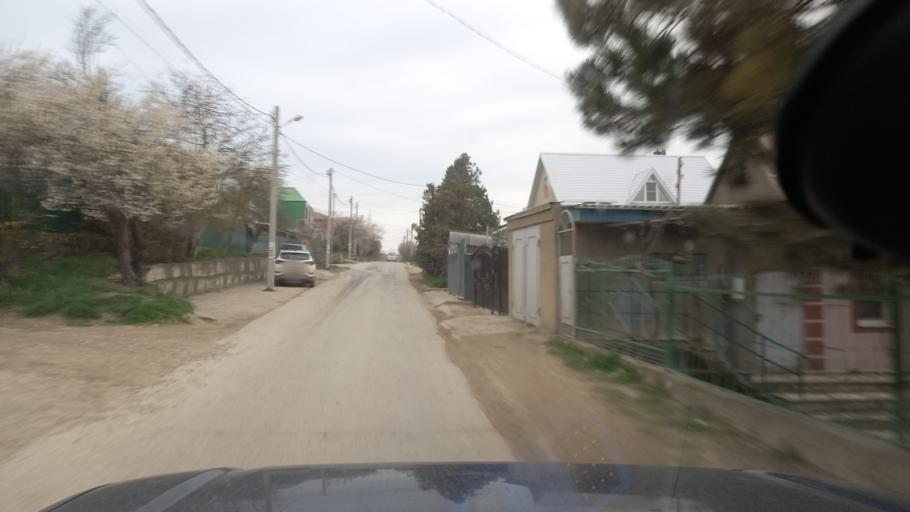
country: RU
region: Krasnodarskiy
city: Anapa
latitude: 44.8503
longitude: 37.3561
